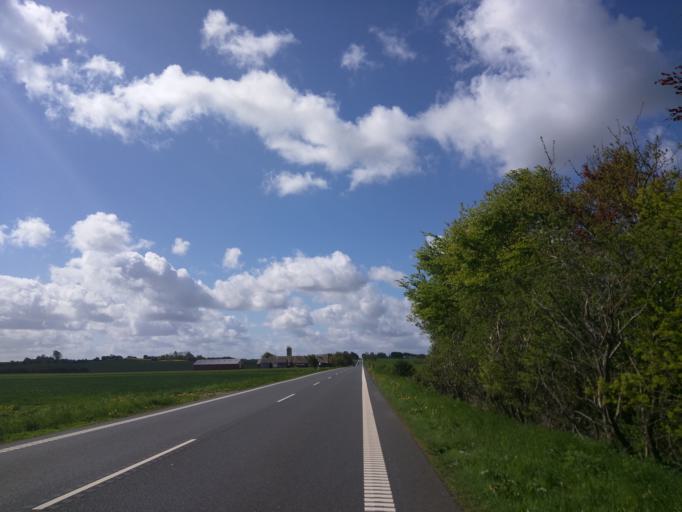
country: DK
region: Central Jutland
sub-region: Silkeborg Kommune
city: Kjellerup
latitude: 56.3661
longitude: 9.4385
